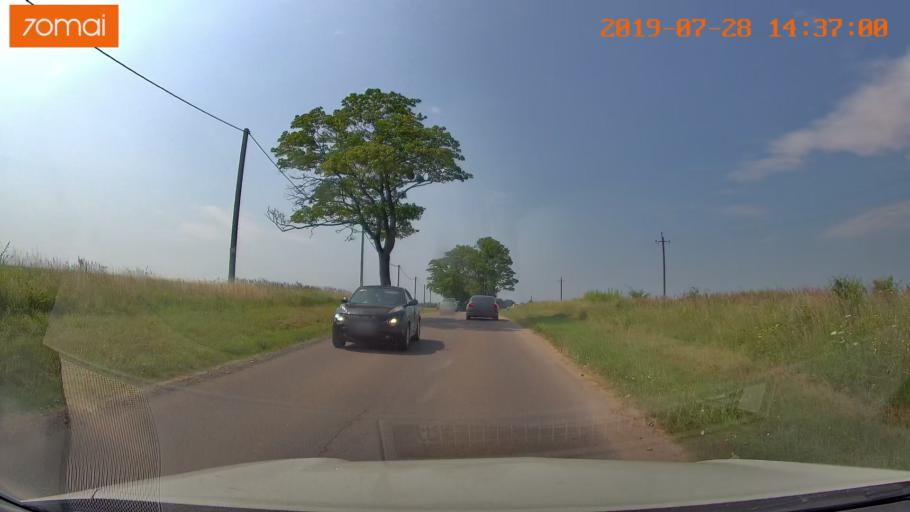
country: RU
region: Kaliningrad
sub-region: Gorod Kaliningrad
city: Yantarnyy
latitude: 54.8401
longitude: 20.0039
